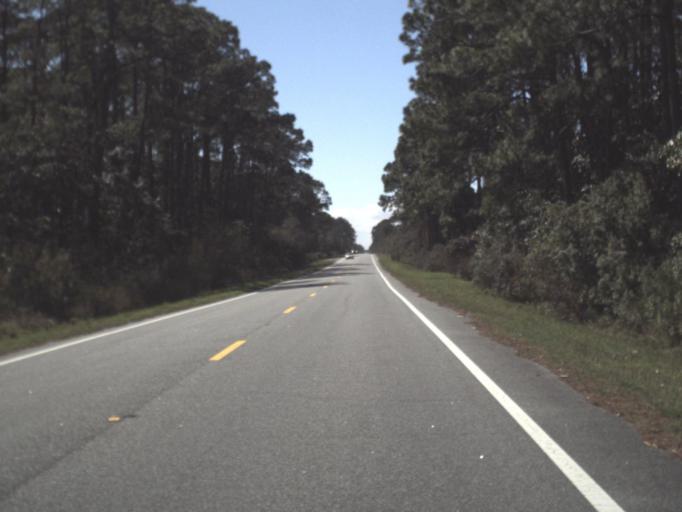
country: US
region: Florida
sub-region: Franklin County
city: Carrabelle
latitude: 29.9269
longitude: -84.4705
